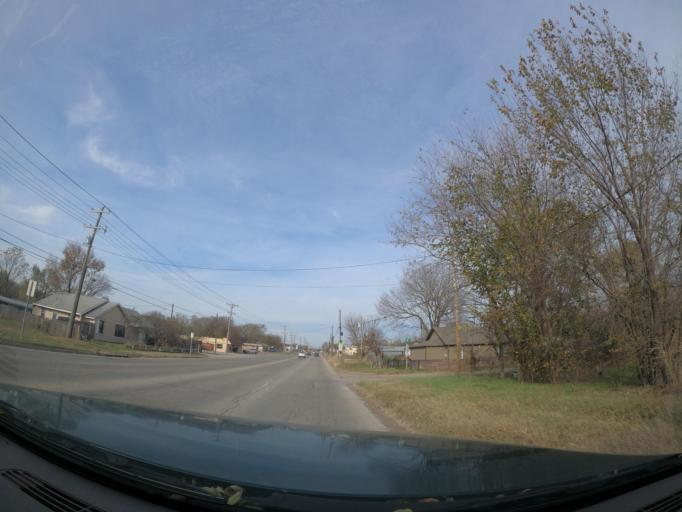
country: US
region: Oklahoma
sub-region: Tulsa County
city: Turley
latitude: 36.2385
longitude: -95.9755
